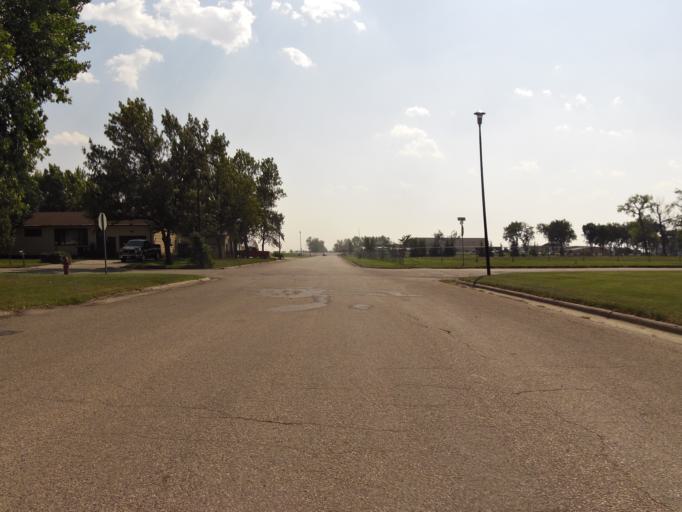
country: US
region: North Dakota
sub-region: Walsh County
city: Grafton
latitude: 48.4147
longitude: -97.3996
